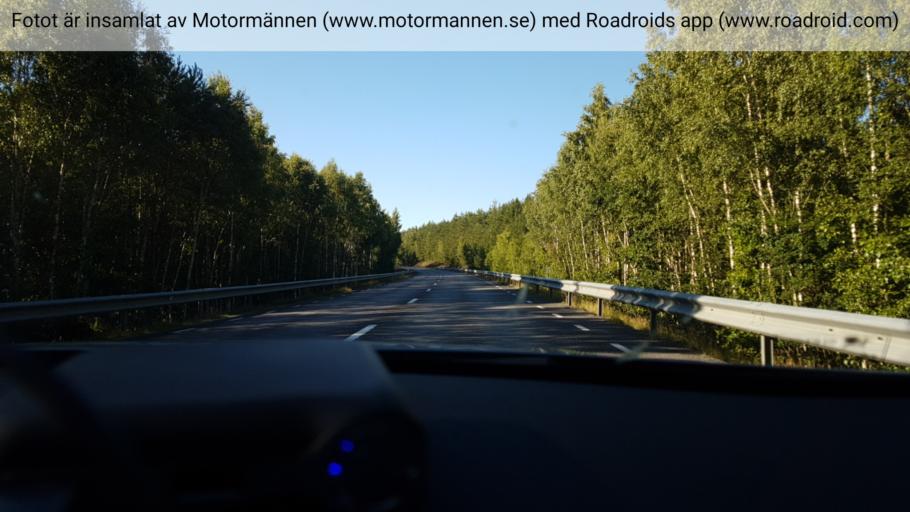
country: SE
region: Joenkoeping
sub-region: Habo Kommun
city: Habo
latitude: 57.9565
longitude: 14.1064
